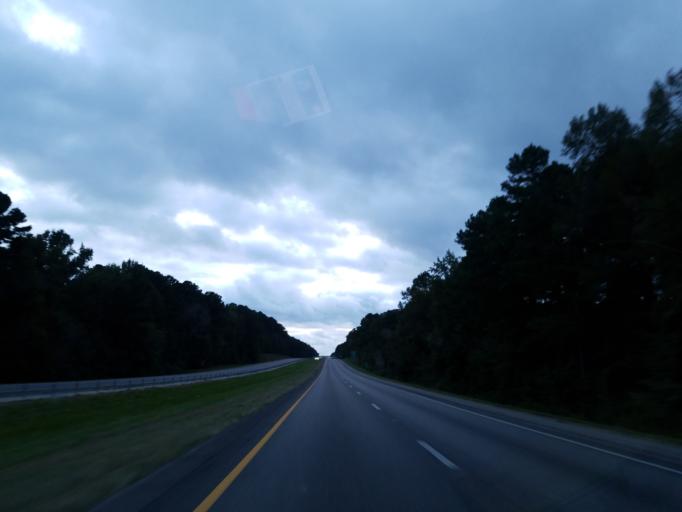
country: US
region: Mississippi
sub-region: Lauderdale County
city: Marion
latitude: 32.3883
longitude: -88.6088
